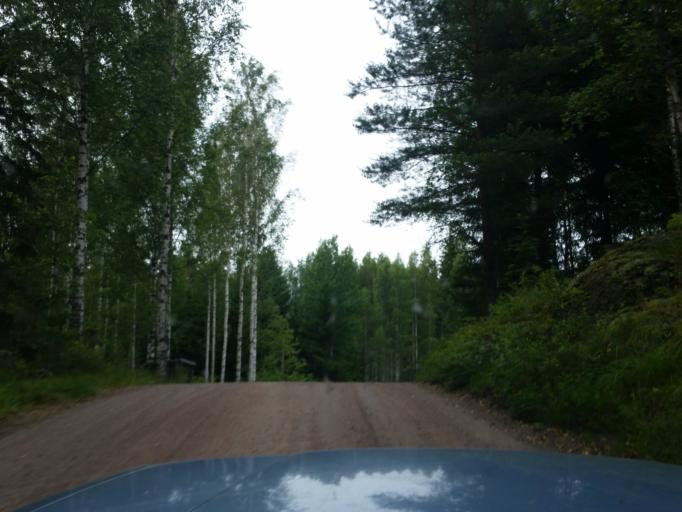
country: FI
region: Uusimaa
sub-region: Helsinki
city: Kaerkoelae
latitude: 60.5690
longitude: 24.0040
